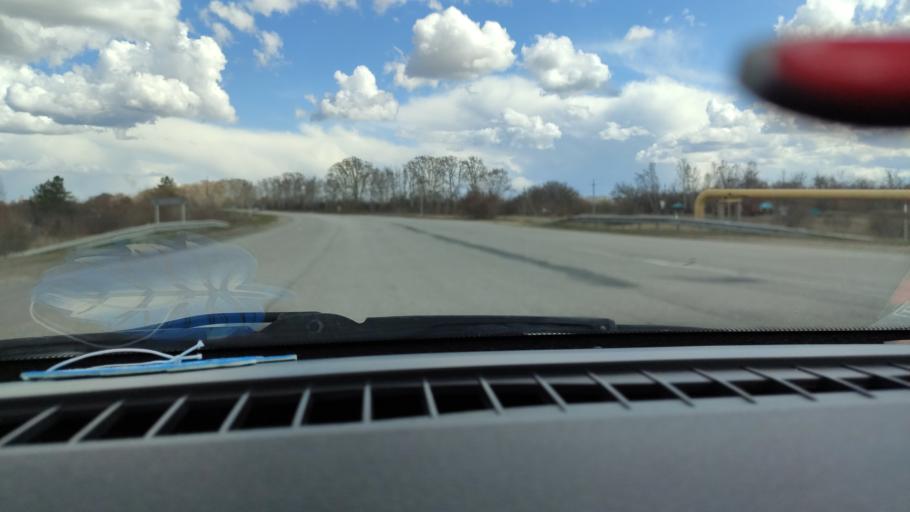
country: RU
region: Samara
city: Varlamovo
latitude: 53.1228
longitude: 48.3022
